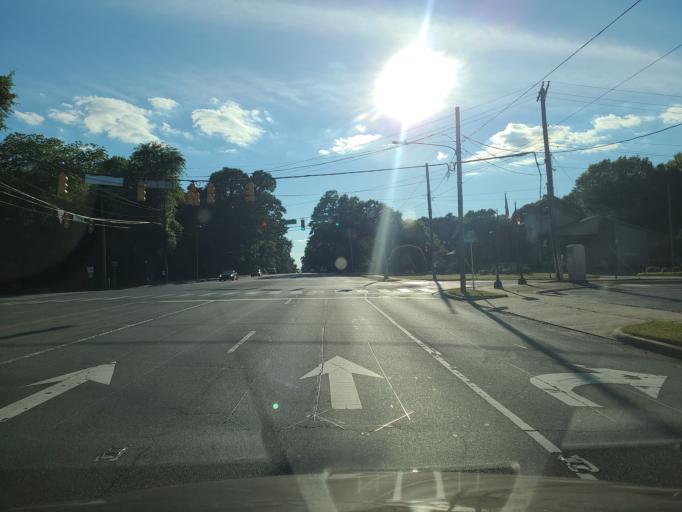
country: US
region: North Carolina
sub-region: Gaston County
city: Gastonia
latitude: 35.2625
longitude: -81.1578
